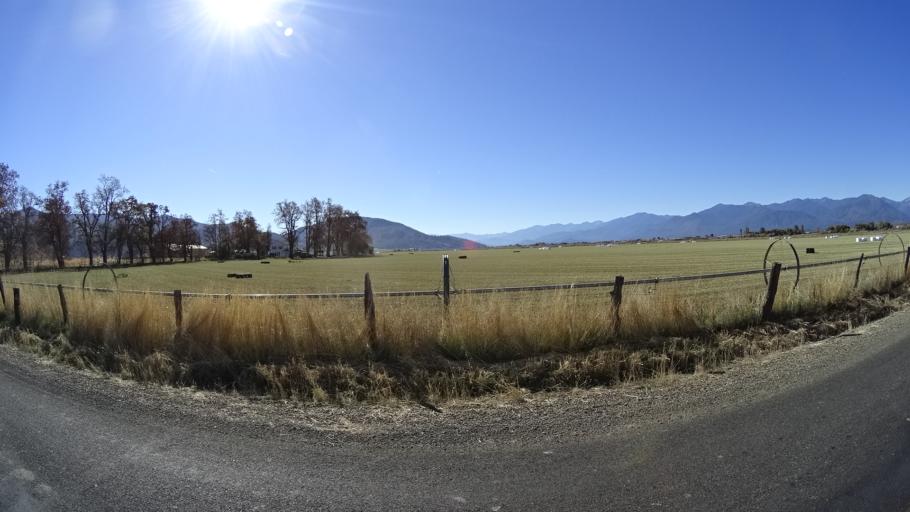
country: US
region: California
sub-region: Siskiyou County
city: Yreka
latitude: 41.5705
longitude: -122.8370
